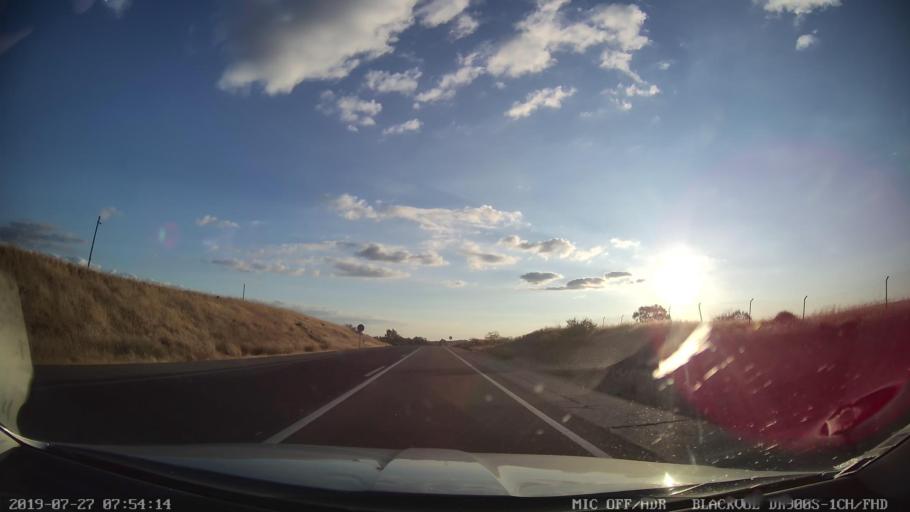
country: ES
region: Extremadura
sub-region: Provincia de Badajoz
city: Trujillanos
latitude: 38.9397
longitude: -6.2958
